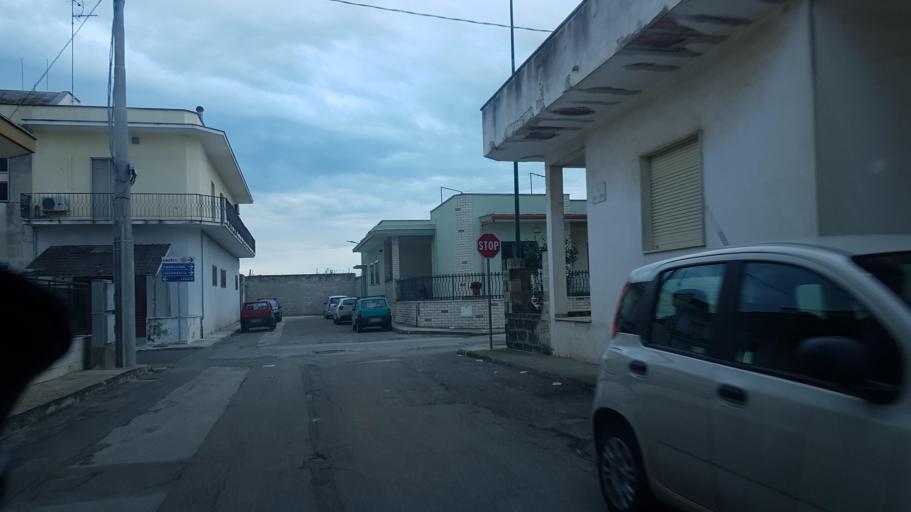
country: IT
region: Apulia
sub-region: Provincia di Lecce
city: Merine
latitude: 40.3361
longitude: 18.2212
